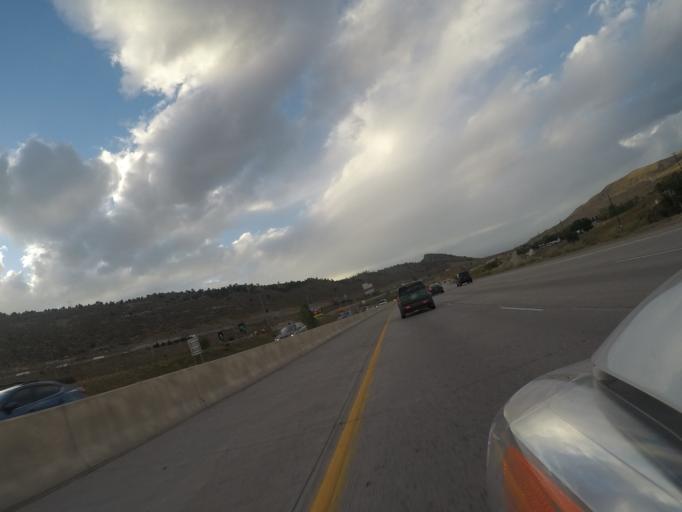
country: US
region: Colorado
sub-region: Jefferson County
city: Indian Hills
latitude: 39.6621
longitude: -105.1846
